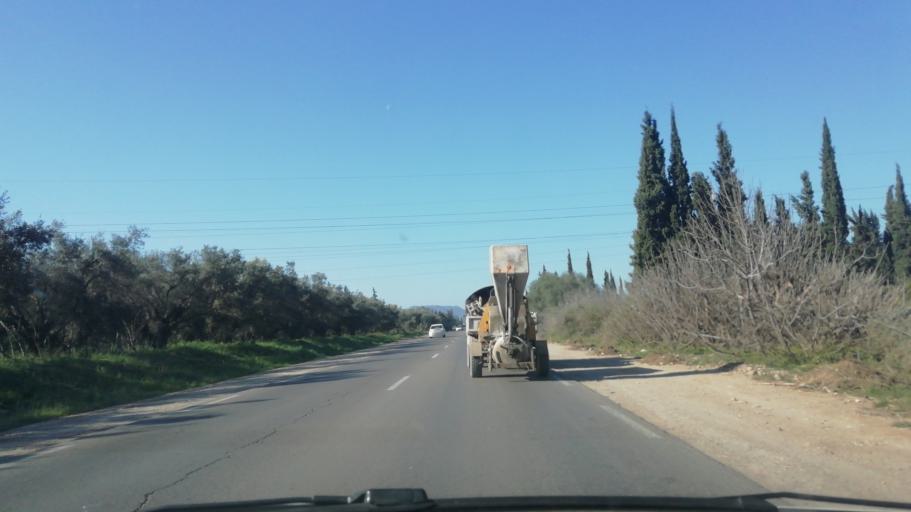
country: DZ
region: Mascara
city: Sig
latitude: 35.5589
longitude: -0.0986
